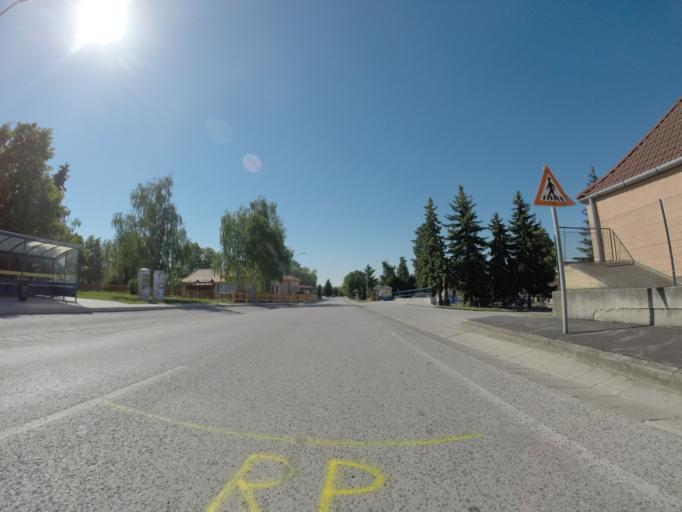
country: SK
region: Trnavsky
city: Hlohovec
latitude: 48.3576
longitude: 17.7959
